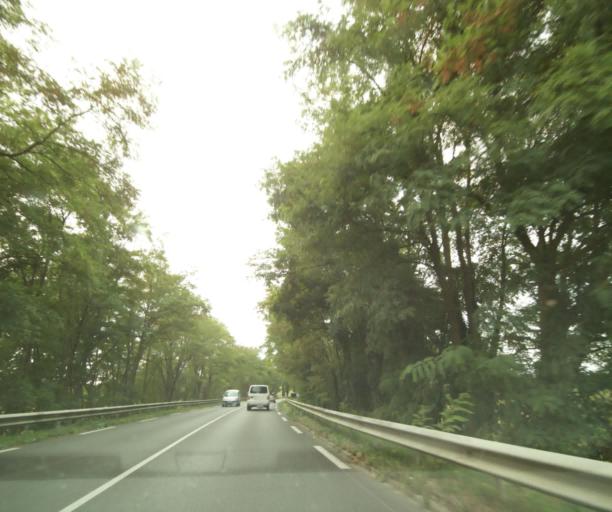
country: FR
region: Centre
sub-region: Departement d'Indre-et-Loire
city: Loches
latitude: 47.1093
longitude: 0.9858
